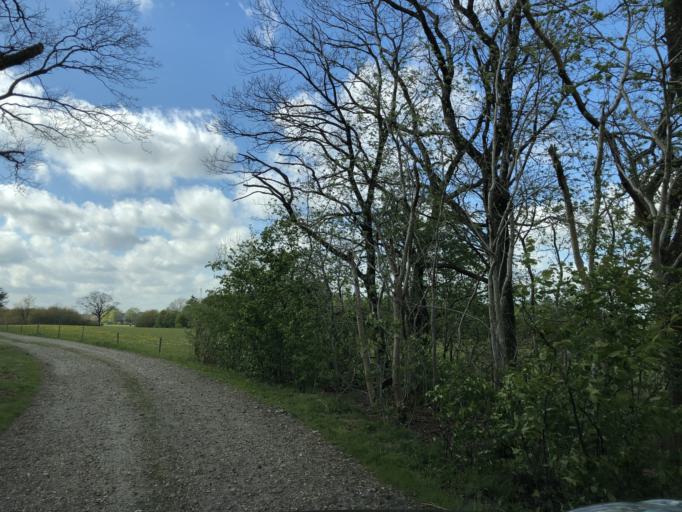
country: DK
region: Central Jutland
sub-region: Herning Kommune
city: Avlum
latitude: 56.2959
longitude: 8.7553
